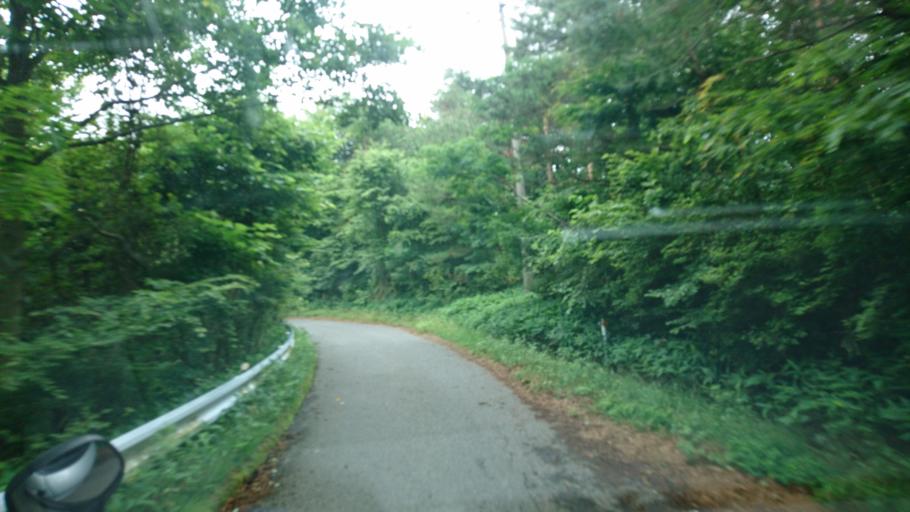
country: JP
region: Iwate
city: Ofunato
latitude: 39.1395
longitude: 141.7548
